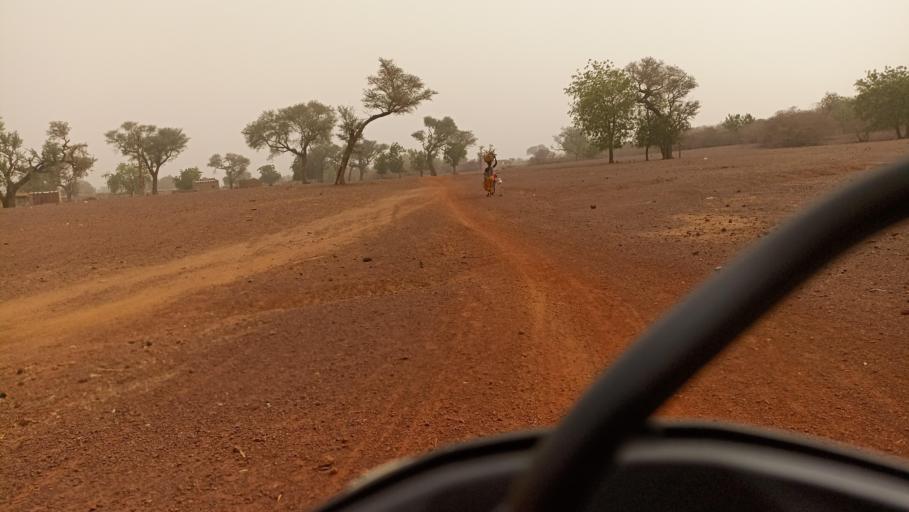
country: BF
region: Nord
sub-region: Province du Zondoma
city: Gourcy
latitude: 13.2964
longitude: -2.5169
